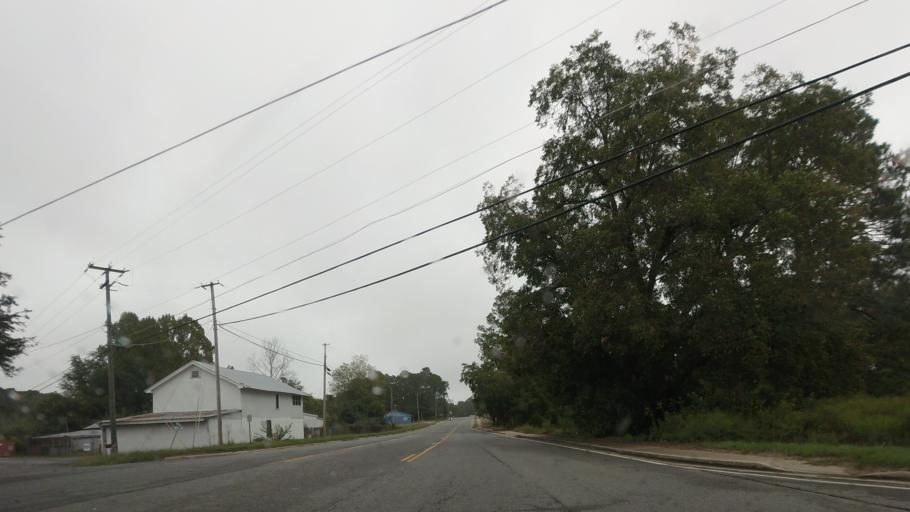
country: US
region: Georgia
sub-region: Ben Hill County
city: Fitzgerald
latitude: 31.7267
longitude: -83.2505
